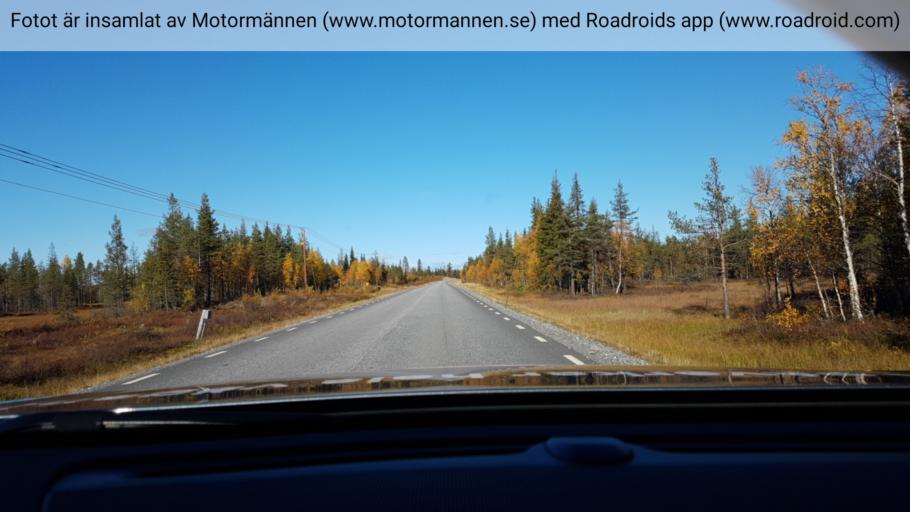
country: SE
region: Norrbotten
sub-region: Gallivare Kommun
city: Gaellivare
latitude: 66.7858
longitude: 21.0416
